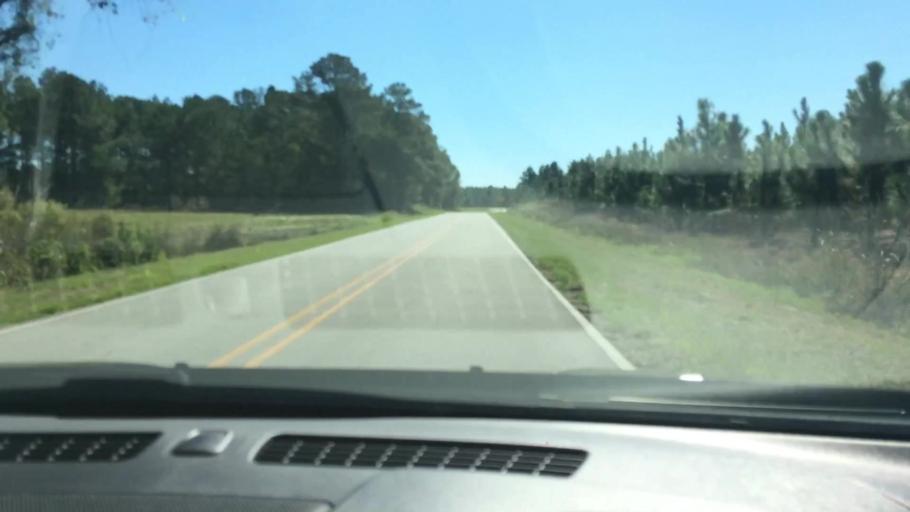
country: US
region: North Carolina
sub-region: Pitt County
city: Grifton
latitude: 35.3318
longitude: -77.3004
